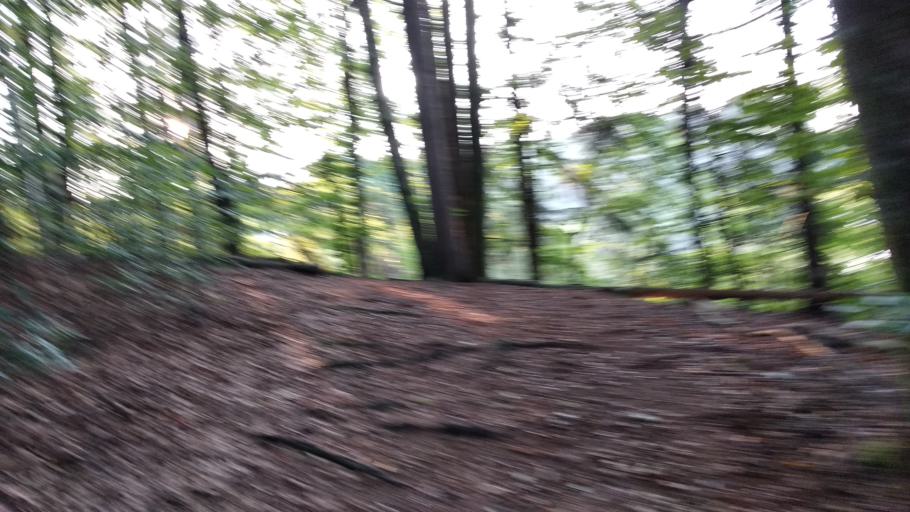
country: DE
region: Bavaria
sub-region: Upper Bavaria
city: Seeon-Seebruck
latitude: 47.9847
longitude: 12.4422
